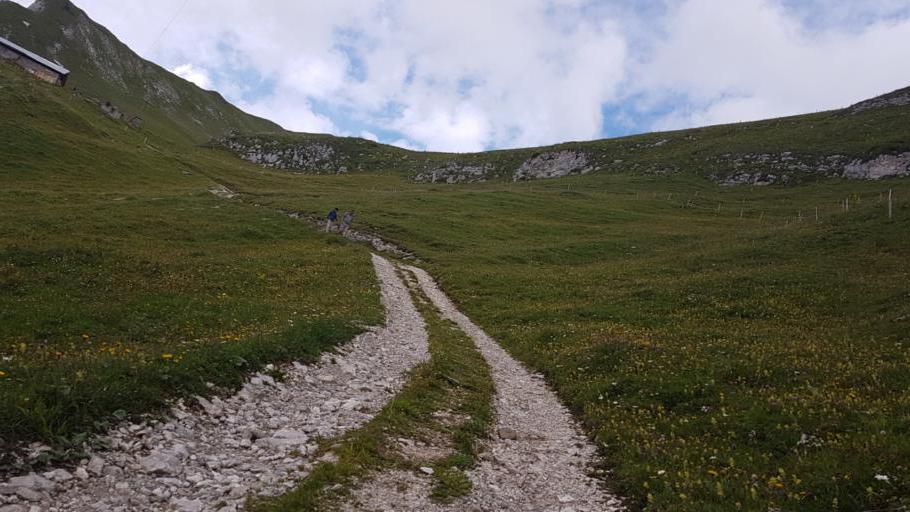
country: CH
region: Bern
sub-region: Obersimmental-Saanen District
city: Boltigen
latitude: 46.6963
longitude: 7.4438
